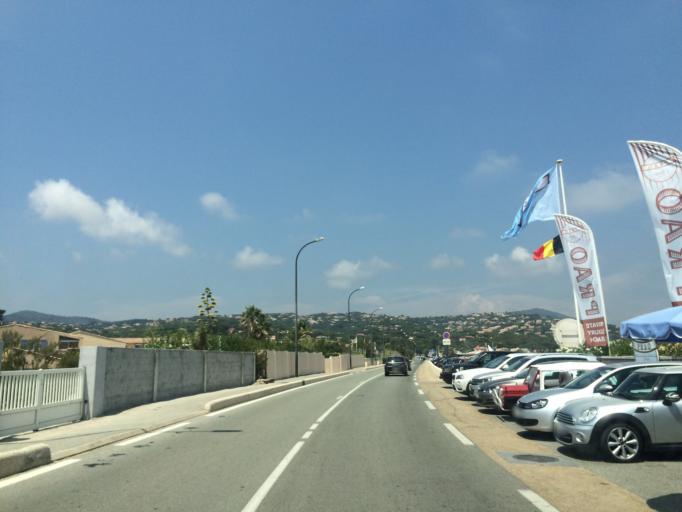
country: FR
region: Provence-Alpes-Cote d'Azur
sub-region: Departement du Var
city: Sainte-Maxime
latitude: 43.3184
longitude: 6.6653
